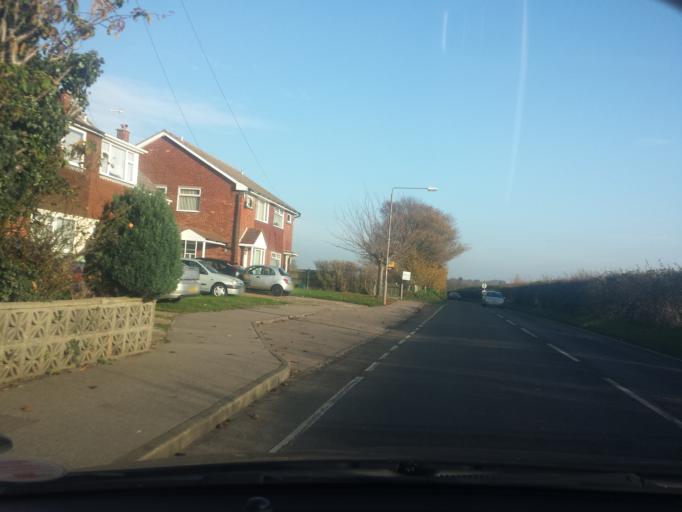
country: GB
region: England
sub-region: Essex
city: Saint Osyth
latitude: 51.8014
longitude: 1.0893
